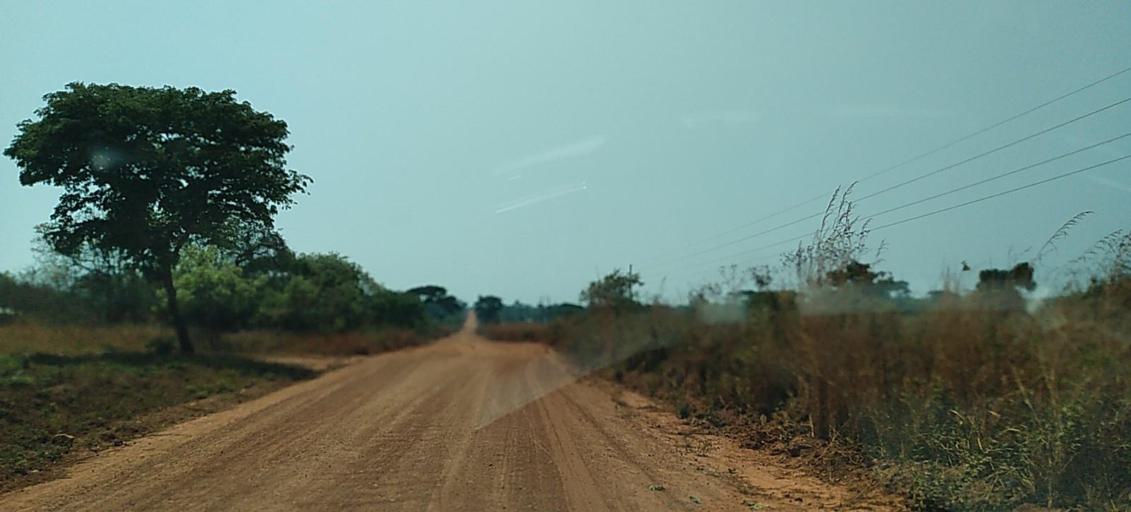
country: ZM
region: North-Western
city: Kansanshi
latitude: -12.0051
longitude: 26.5656
